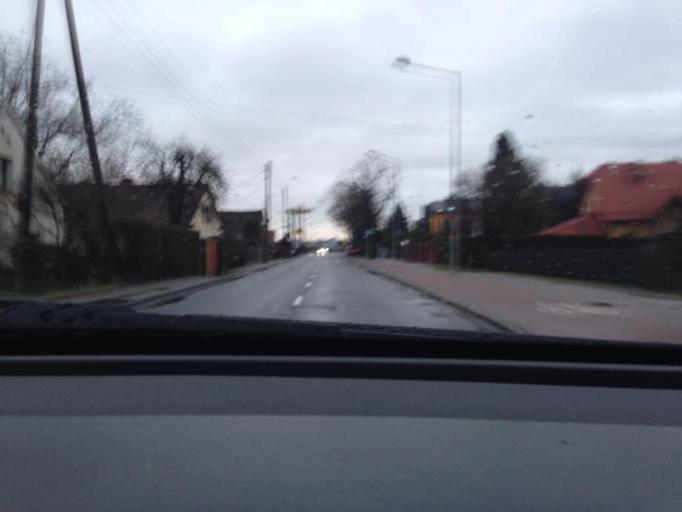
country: PL
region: Opole Voivodeship
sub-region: Powiat opolski
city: Opole
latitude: 50.6783
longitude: 17.9592
